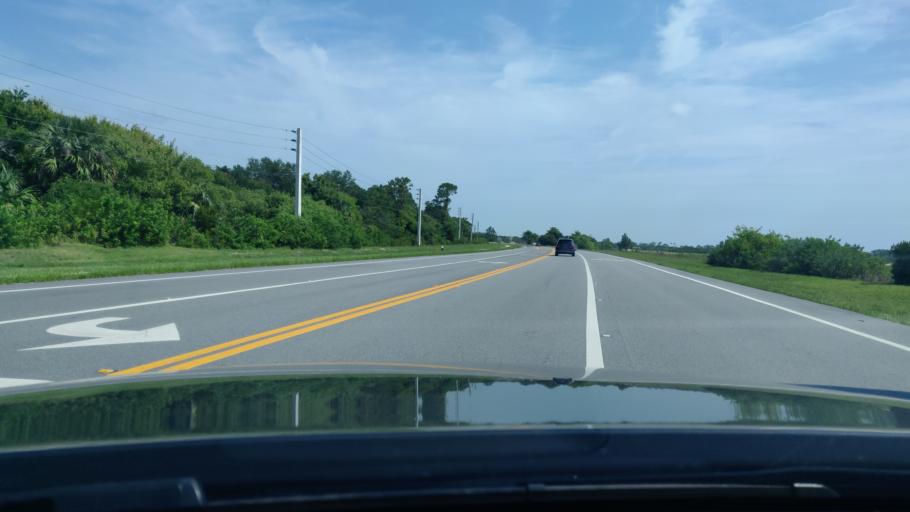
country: US
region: Florida
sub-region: Flagler County
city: Flagler Beach
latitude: 29.4942
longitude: -81.1572
